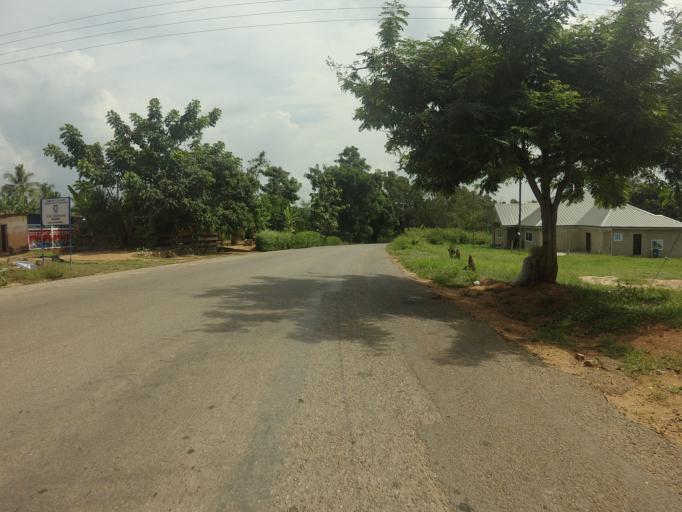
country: GH
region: Eastern
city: Aburi
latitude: 5.9673
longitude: -0.2195
